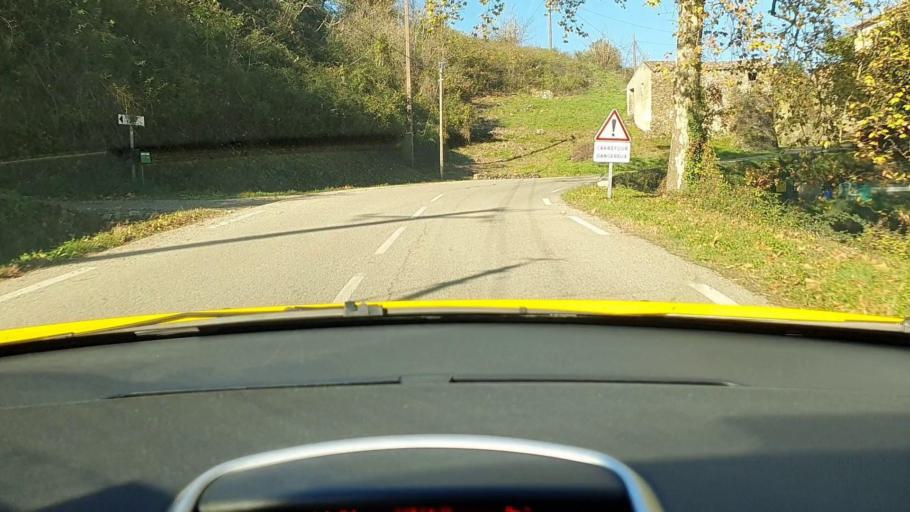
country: FR
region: Languedoc-Roussillon
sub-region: Departement du Gard
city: Sumene
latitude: 43.9865
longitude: 3.7020
